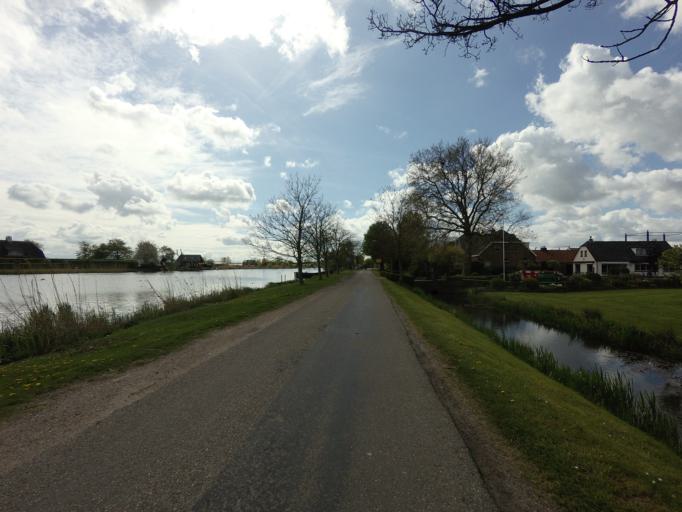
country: NL
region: North Holland
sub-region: Gemeente Weesp
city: Weesp
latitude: 52.2784
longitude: 5.0422
